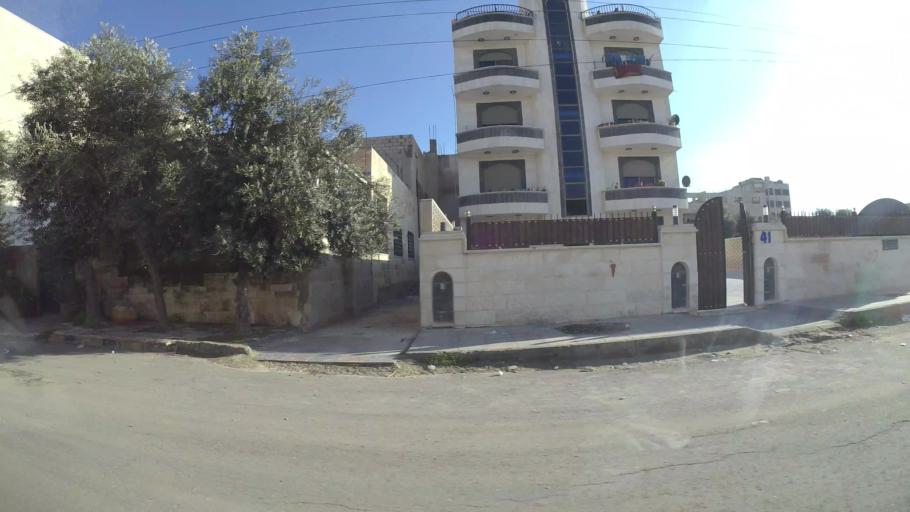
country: JO
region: Amman
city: Al Bunayyat ash Shamaliyah
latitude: 31.9014
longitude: 35.9134
